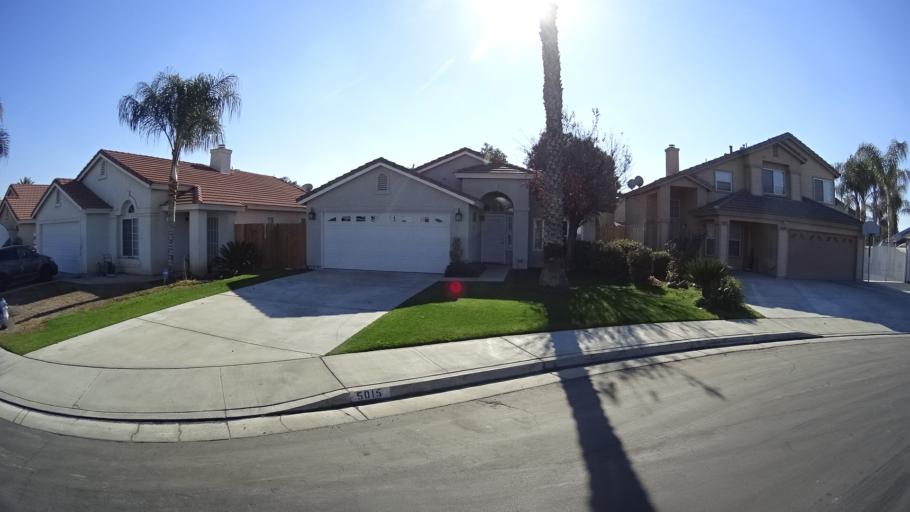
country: US
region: California
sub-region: Kern County
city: Greenfield
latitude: 35.3003
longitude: -119.0585
